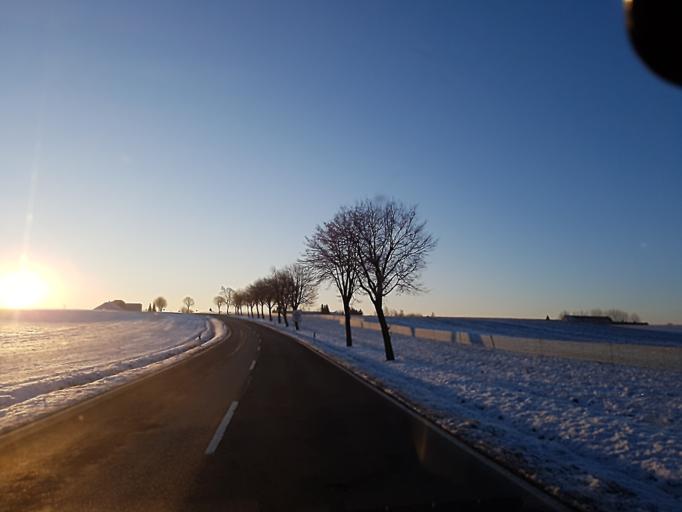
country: DE
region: Saxony
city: Grossweitzschen
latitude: 51.1647
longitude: 13.0458
